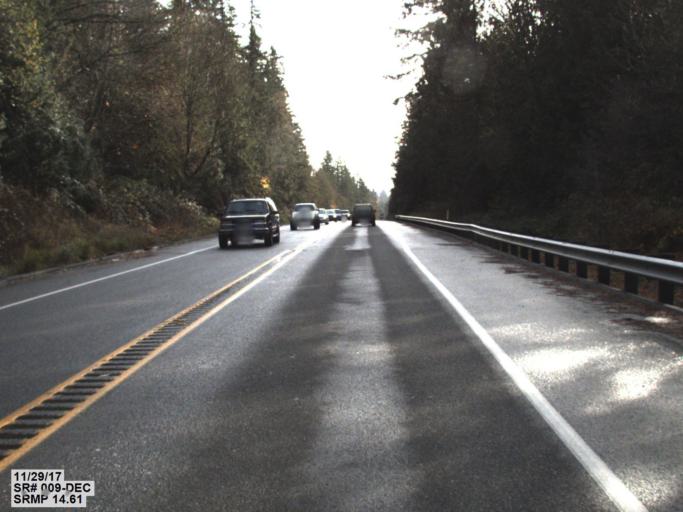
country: US
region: Washington
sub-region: Snohomish County
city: West Lake Stevens
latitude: 47.9863
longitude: -122.1036
